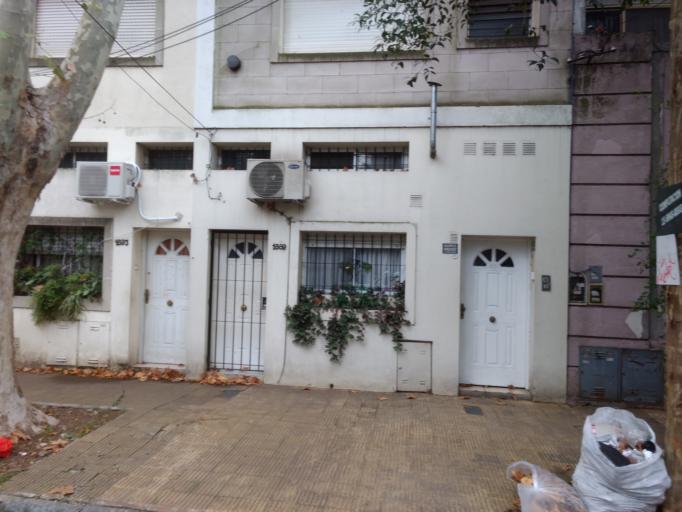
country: AR
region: Buenos Aires
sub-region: Partido de Vicente Lopez
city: Olivos
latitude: -34.5137
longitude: -58.4951
